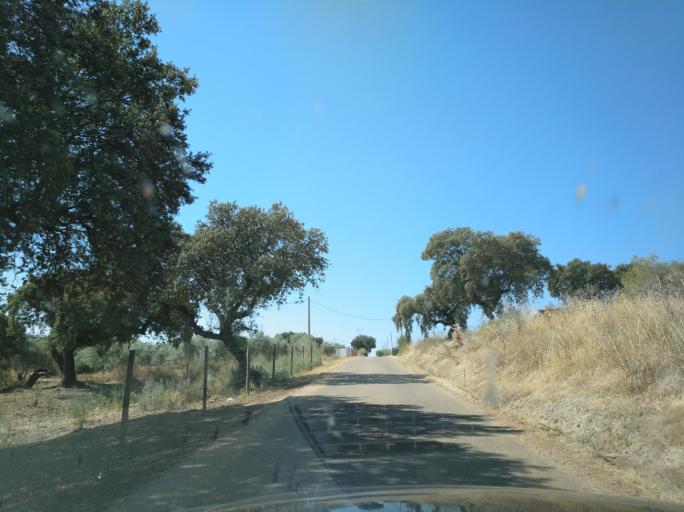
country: PT
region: Portalegre
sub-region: Campo Maior
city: Campo Maior
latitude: 39.0484
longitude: -7.0006
